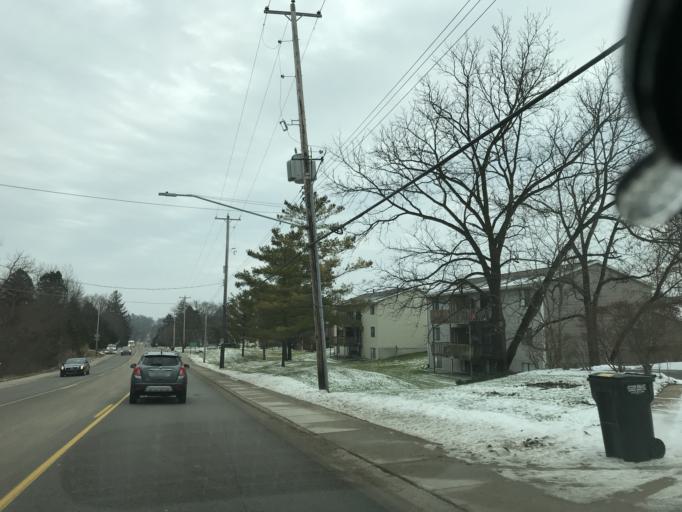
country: US
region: Michigan
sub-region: Kent County
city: Rockford
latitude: 43.1173
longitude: -85.5696
